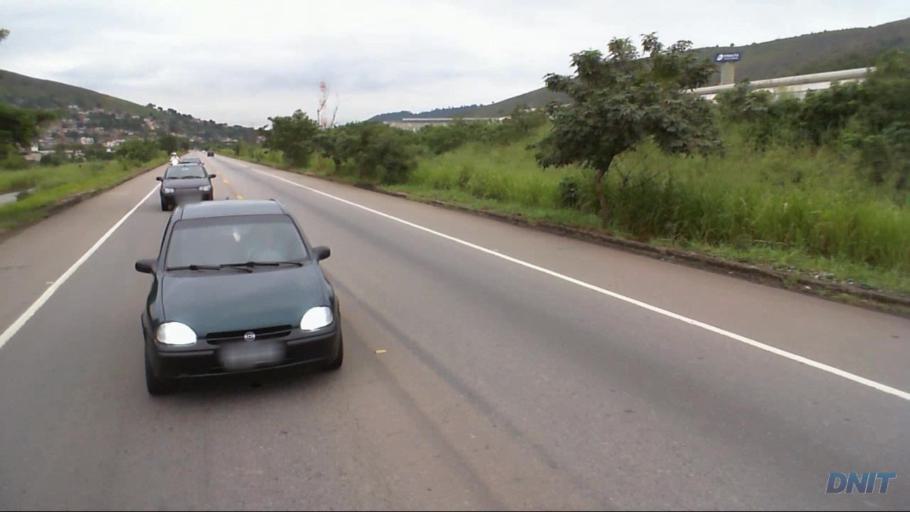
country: BR
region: Minas Gerais
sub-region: Coronel Fabriciano
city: Coronel Fabriciano
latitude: -19.5300
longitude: -42.6115
